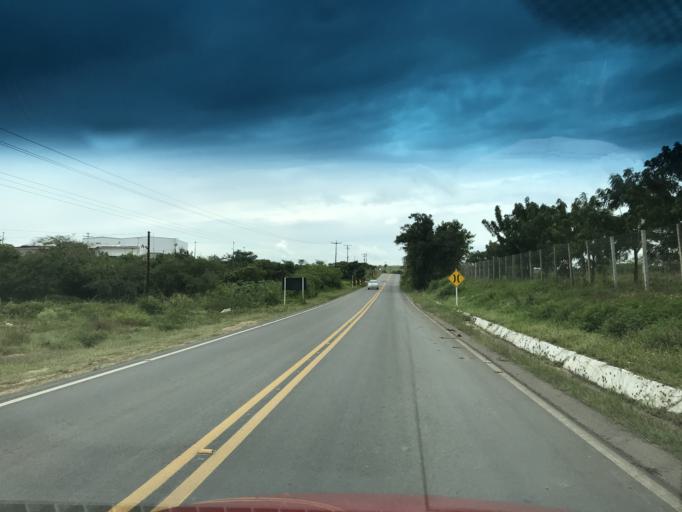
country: BR
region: Bahia
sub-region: Castro Alves
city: Castro Alves
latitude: -12.7594
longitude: -39.4184
